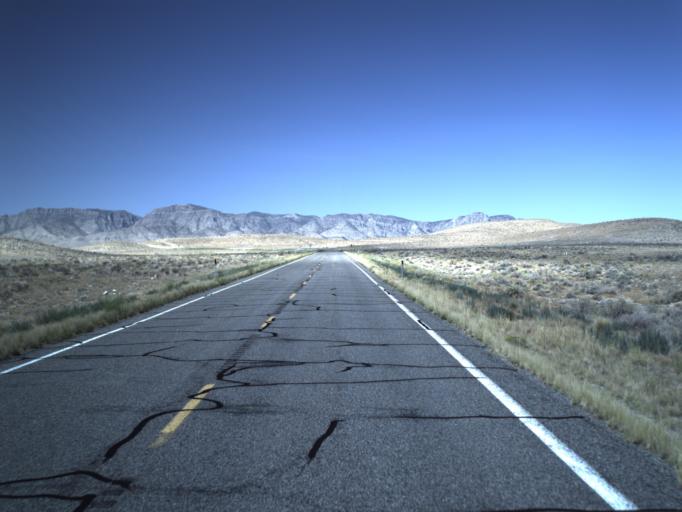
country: US
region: Utah
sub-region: Beaver County
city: Milford
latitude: 39.0369
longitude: -113.3294
